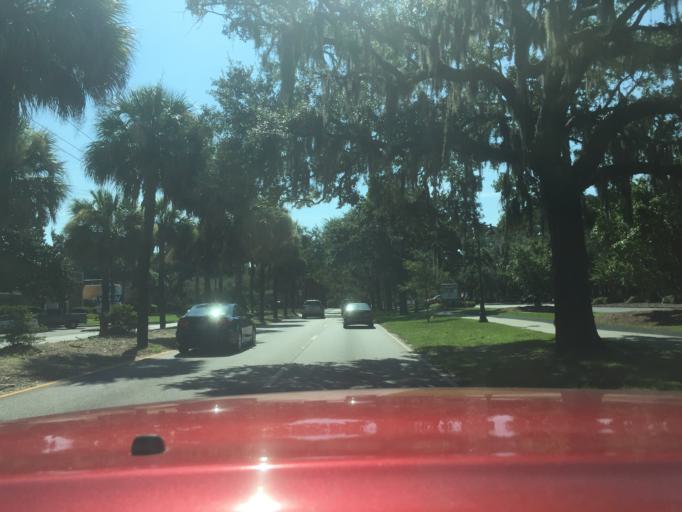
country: US
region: Georgia
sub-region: Chatham County
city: Thunderbolt
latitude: 32.0465
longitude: -81.0793
